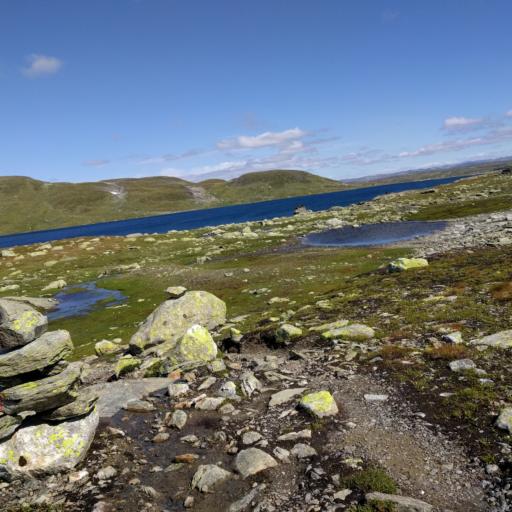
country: NO
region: Aust-Agder
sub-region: Bykle
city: Hovden
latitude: 59.8687
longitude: 7.2160
